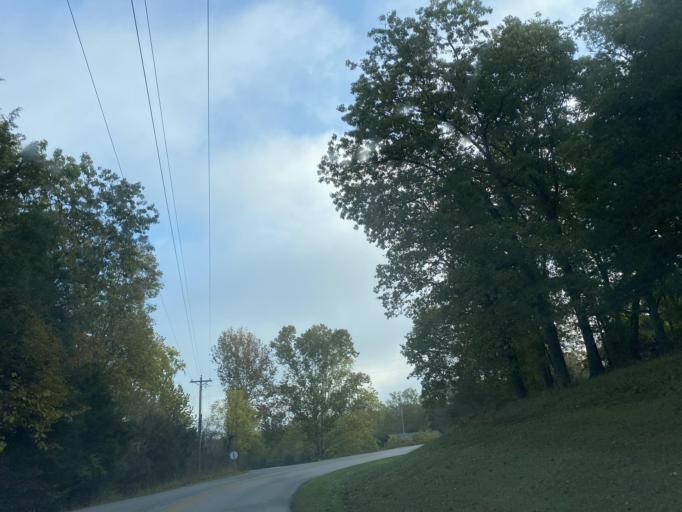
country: US
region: Kentucky
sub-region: Pendleton County
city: Falmouth
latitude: 38.7252
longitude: -84.2846
